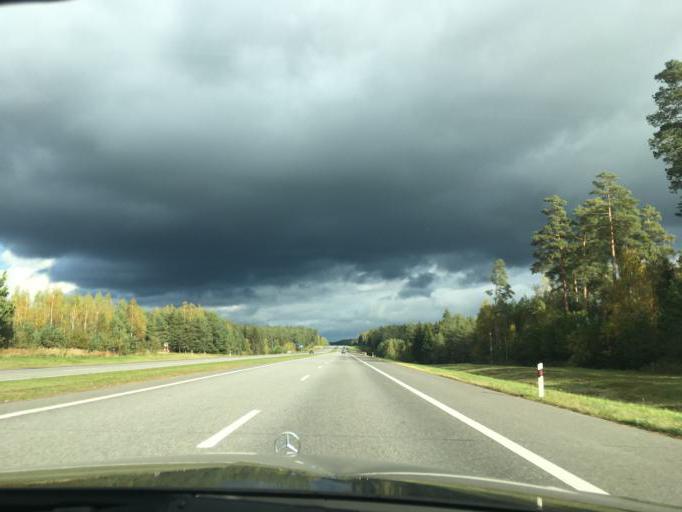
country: BY
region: Minsk
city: Bobr
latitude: 54.4025
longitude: 29.4658
